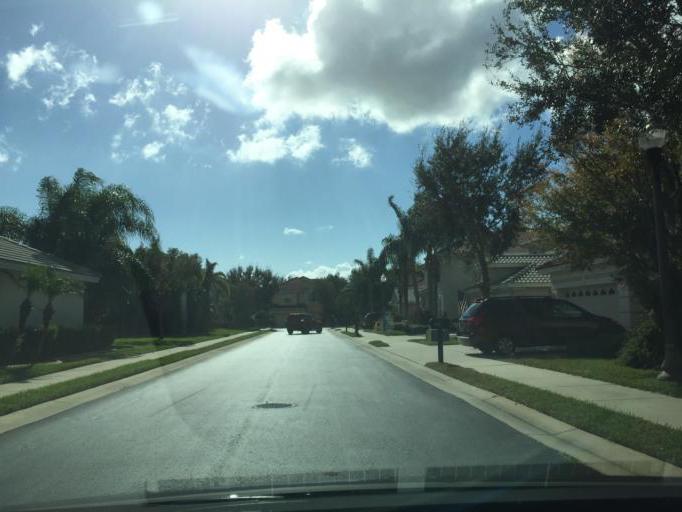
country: US
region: Florida
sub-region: Pinellas County
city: Saint George
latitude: 28.0436
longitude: -82.7436
